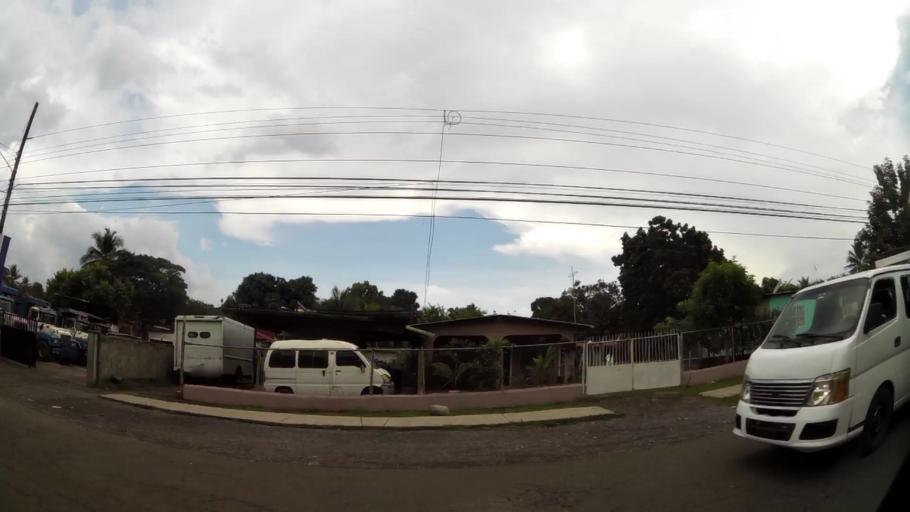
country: PA
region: Panama
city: Cabra Numero Uno
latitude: 9.1117
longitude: -79.3413
